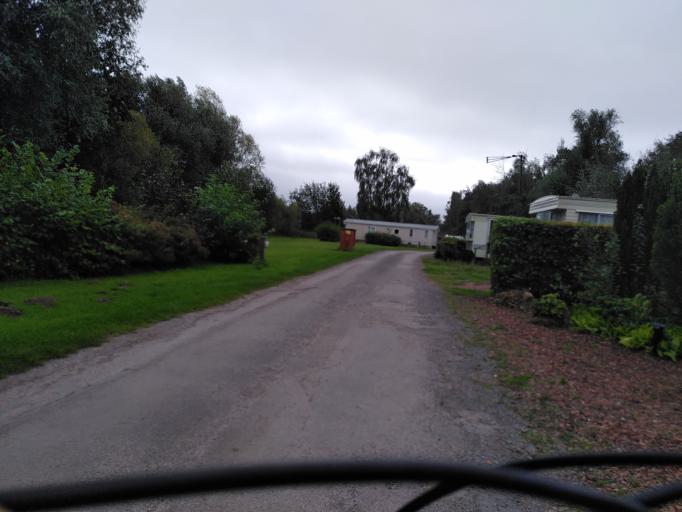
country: FR
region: Nord-Pas-de-Calais
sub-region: Departement du Pas-de-Calais
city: Mametz
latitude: 50.6413
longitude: 2.3008
